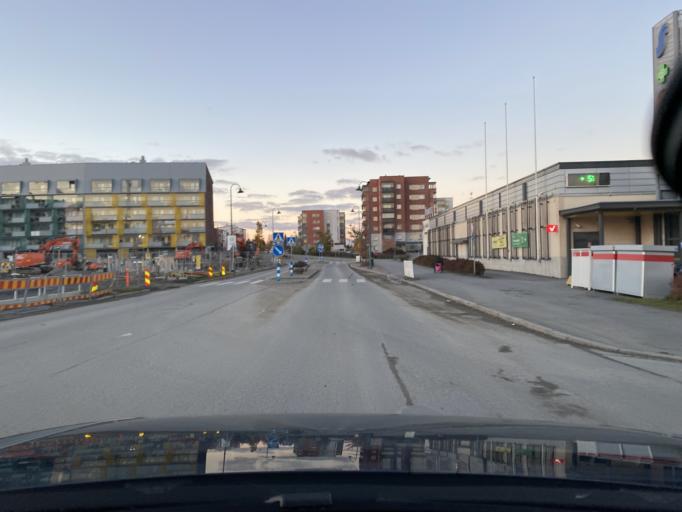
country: FI
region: Pirkanmaa
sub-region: Tampere
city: Lempaeaelae
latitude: 61.3132
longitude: 23.7588
